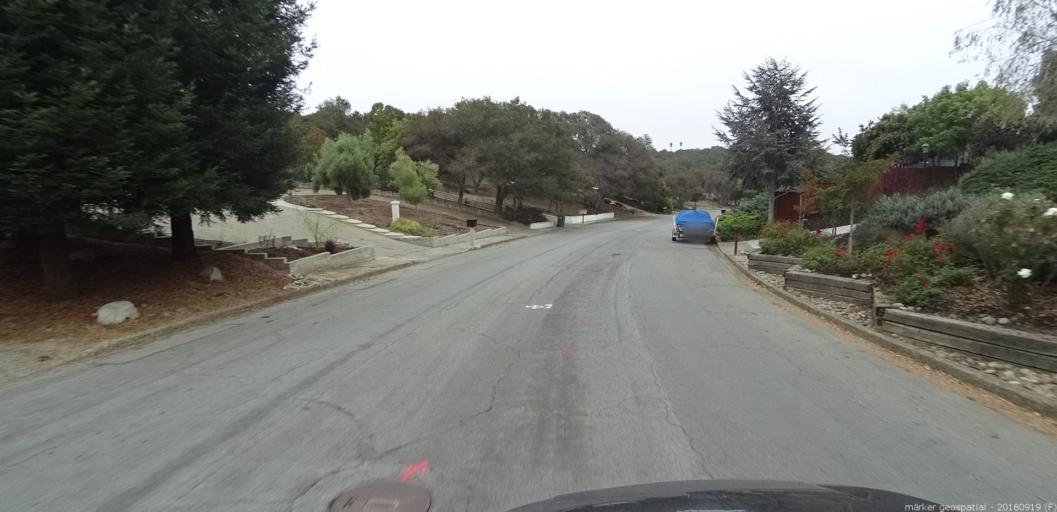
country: US
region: California
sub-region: Monterey County
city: Prunedale
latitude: 36.7822
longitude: -121.7150
